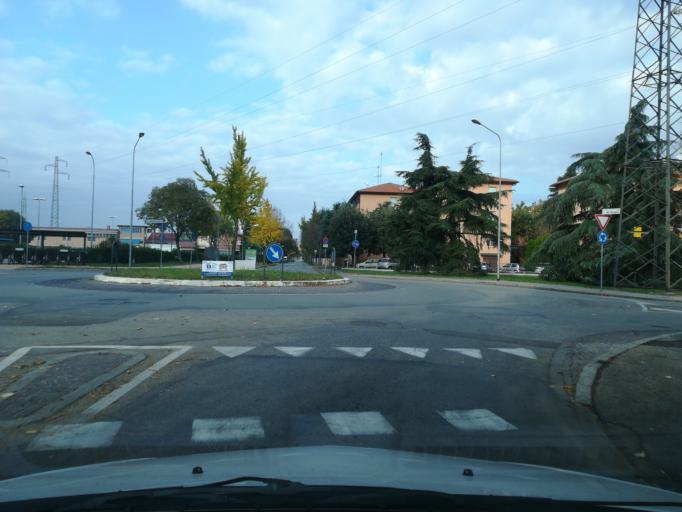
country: IT
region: Emilia-Romagna
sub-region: Provincia di Bologna
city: Imola
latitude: 44.3620
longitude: 11.7210
